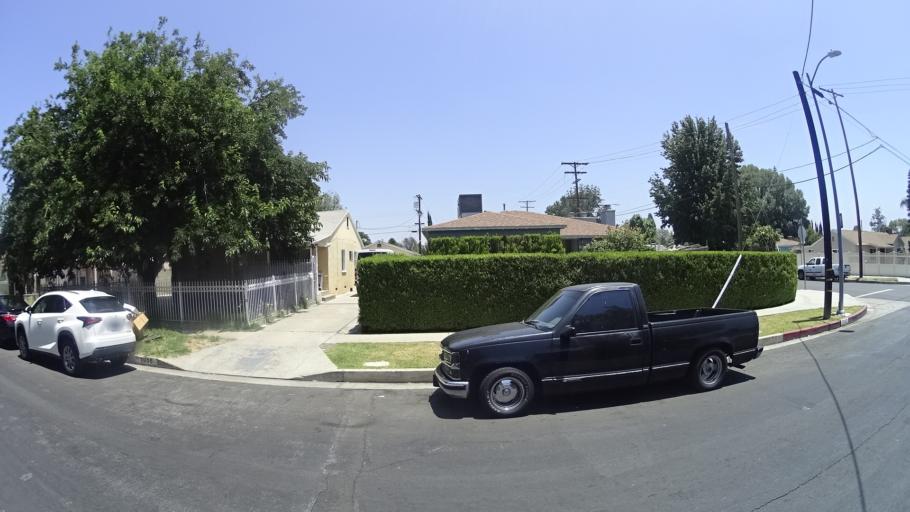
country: US
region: California
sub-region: Los Angeles County
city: Van Nuys
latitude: 34.1977
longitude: -118.4445
